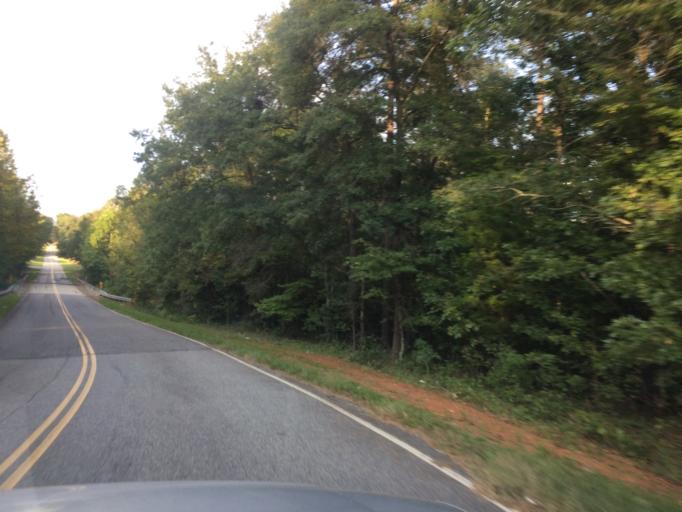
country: US
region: South Carolina
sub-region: Anderson County
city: Piedmont
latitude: 34.6859
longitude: -82.5053
